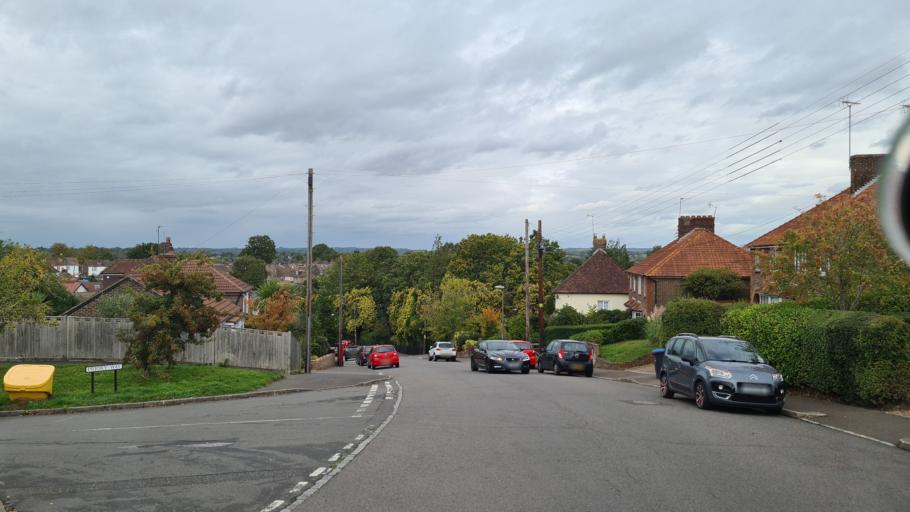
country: GB
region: England
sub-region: West Sussex
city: Haywards Heath
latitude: 50.9976
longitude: -0.0925
